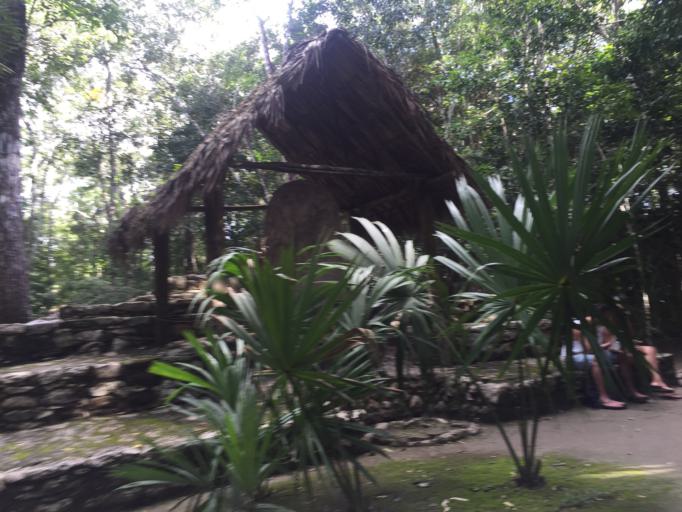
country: MX
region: Quintana Roo
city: Coba
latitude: 20.4833
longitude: -87.7223
